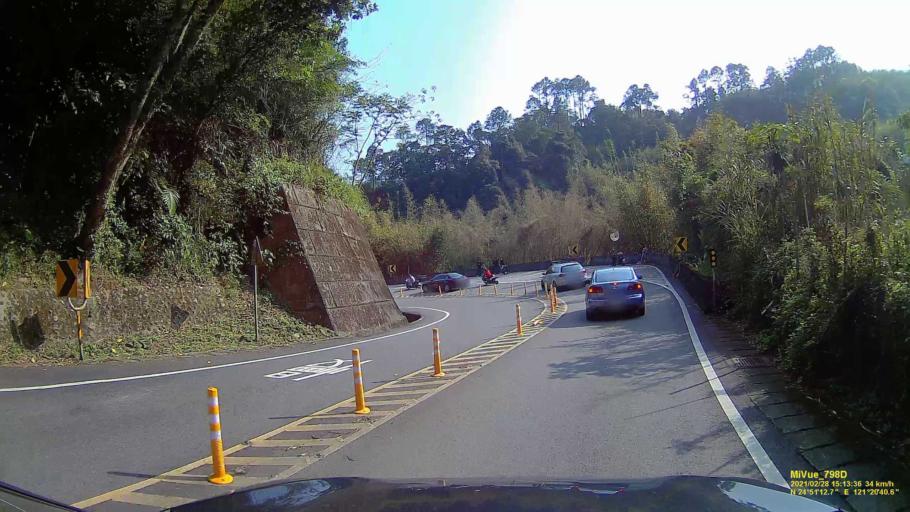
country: TW
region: Taiwan
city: Daxi
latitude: 24.8535
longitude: 121.3446
